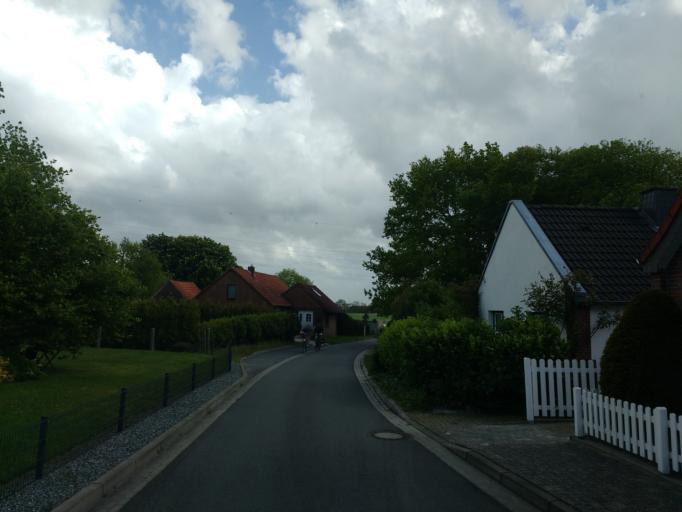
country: DE
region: Lower Saxony
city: Jever
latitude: 53.6662
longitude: 7.9300
